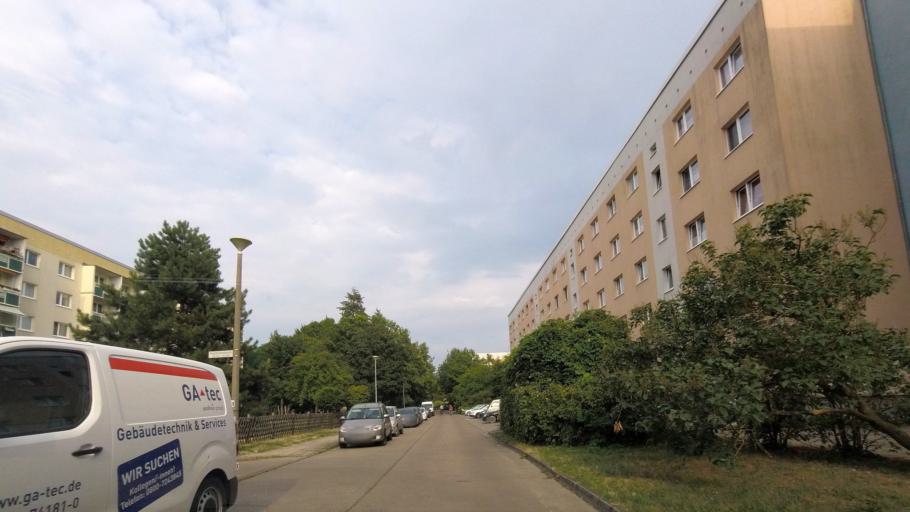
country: DE
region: Berlin
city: Wannsee
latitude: 52.3841
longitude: 13.1349
